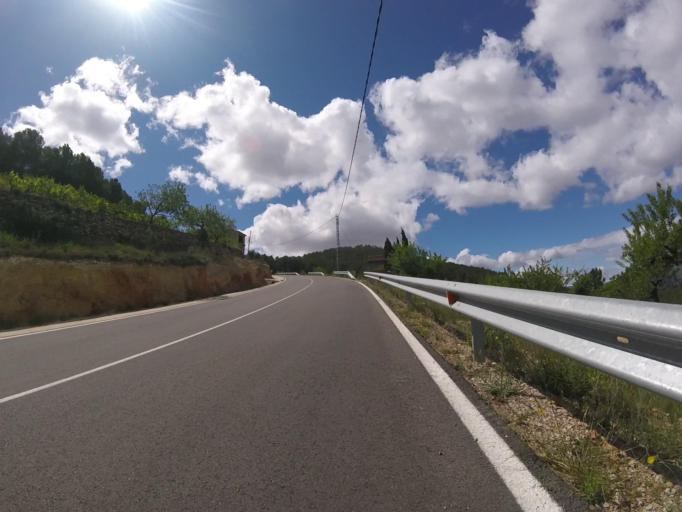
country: ES
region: Valencia
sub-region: Provincia de Castello
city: Culla
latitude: 40.2759
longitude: -0.1114
